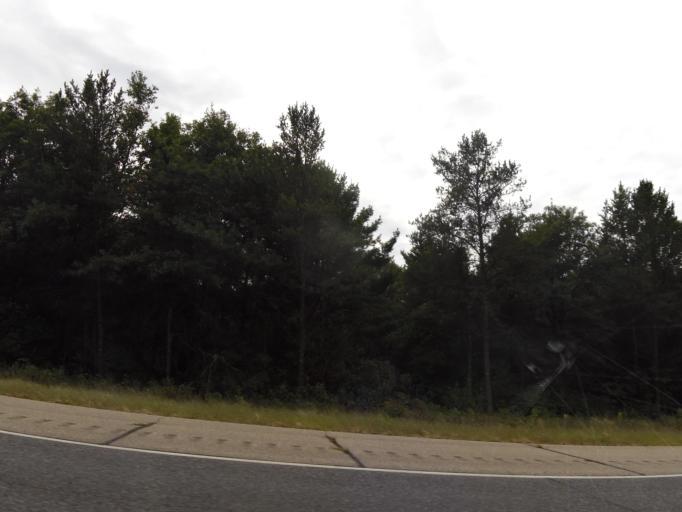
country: US
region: Wisconsin
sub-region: Monroe County
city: Sparta
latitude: 43.9413
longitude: -90.6685
